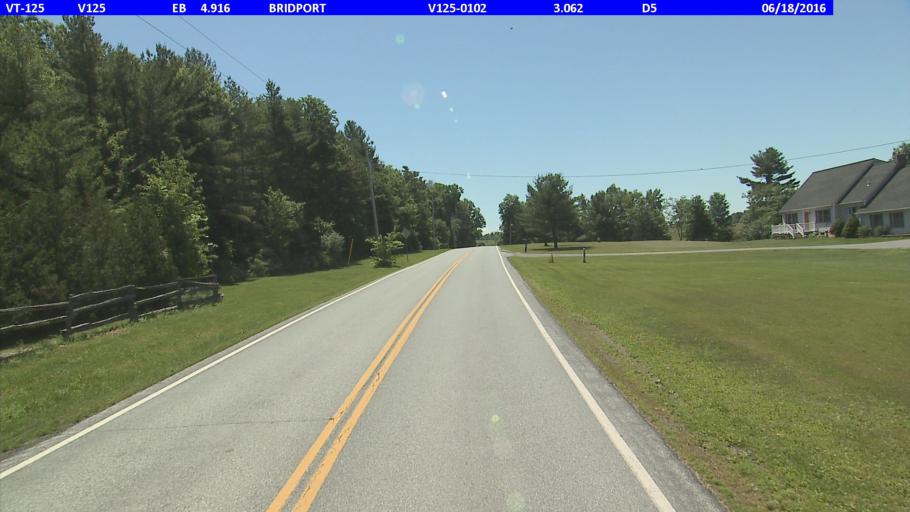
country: US
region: New York
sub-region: Essex County
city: Port Henry
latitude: 43.9958
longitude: -73.3508
